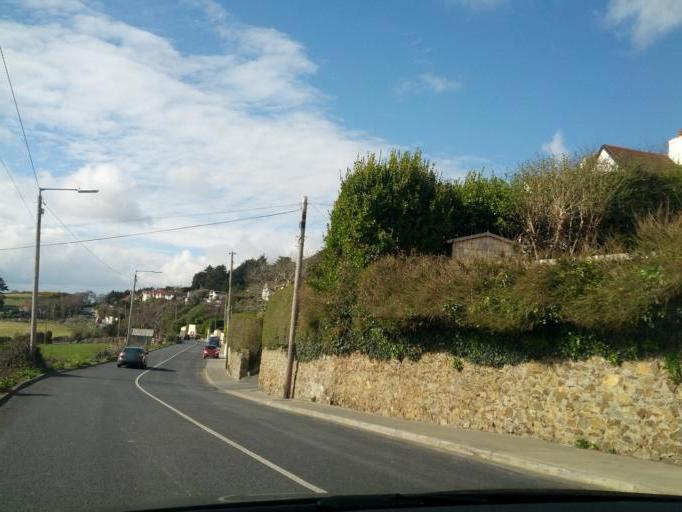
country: IE
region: Leinster
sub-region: Fingal County
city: Howth
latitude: 53.3674
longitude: -6.0803
